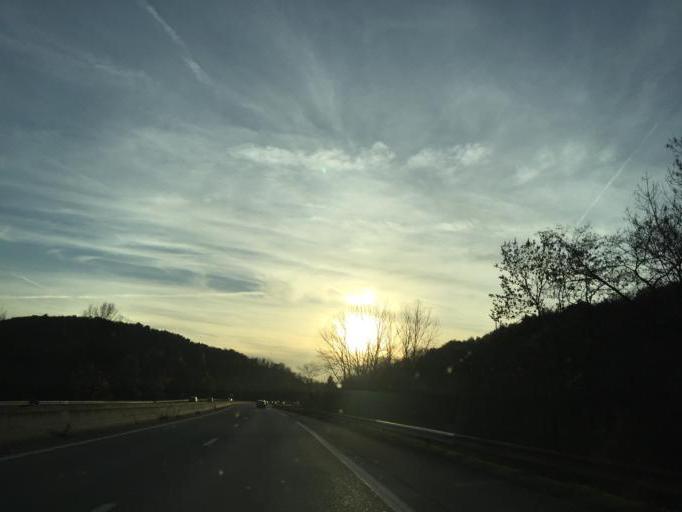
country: FR
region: Rhone-Alpes
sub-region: Departement du Rhone
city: Echalas
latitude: 45.5616
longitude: 4.6963
